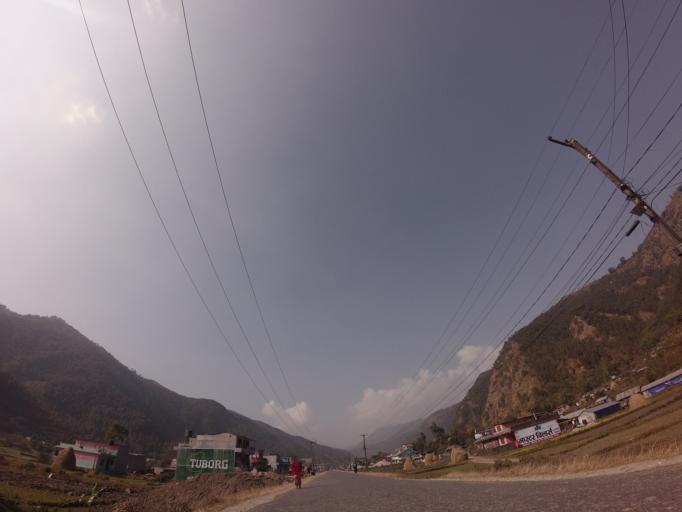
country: NP
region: Western Region
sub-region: Gandaki Zone
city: Pokhara
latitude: 28.2853
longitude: 83.9056
